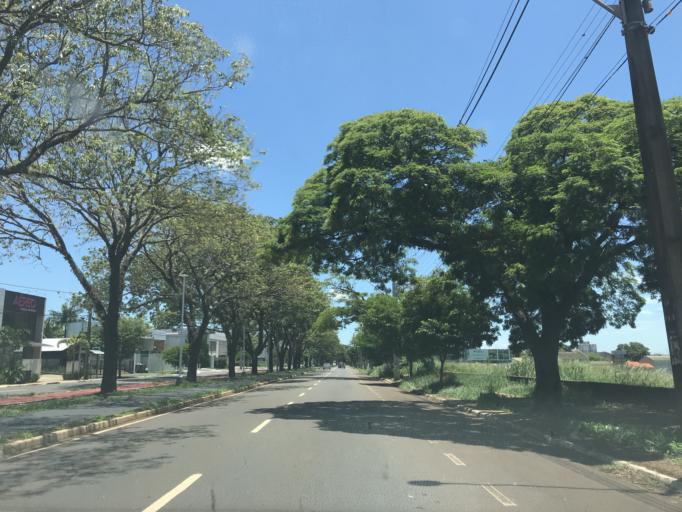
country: BR
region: Parana
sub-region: Maringa
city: Maringa
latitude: -23.4500
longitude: -51.9155
